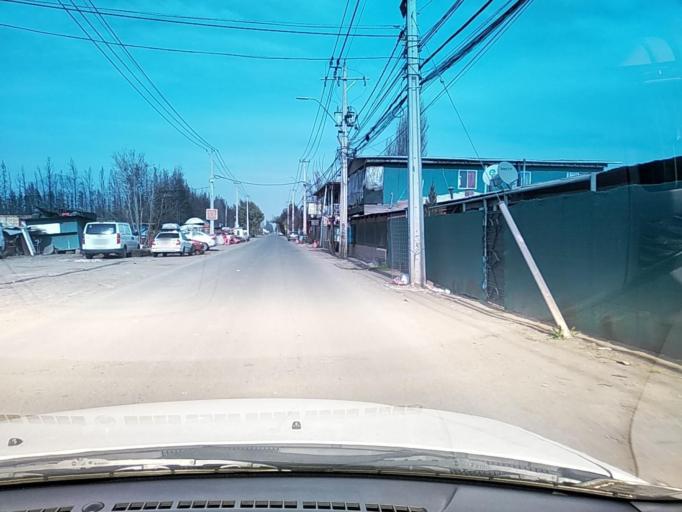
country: CL
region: Santiago Metropolitan
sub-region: Provincia de Chacabuco
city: Chicureo Abajo
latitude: -33.2854
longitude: -70.7300
